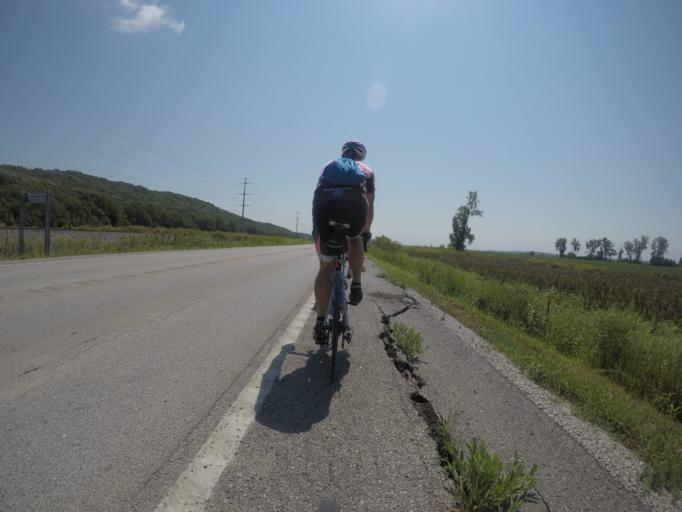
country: US
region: Missouri
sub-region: Platte County
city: Weston
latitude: 39.4487
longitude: -94.9555
